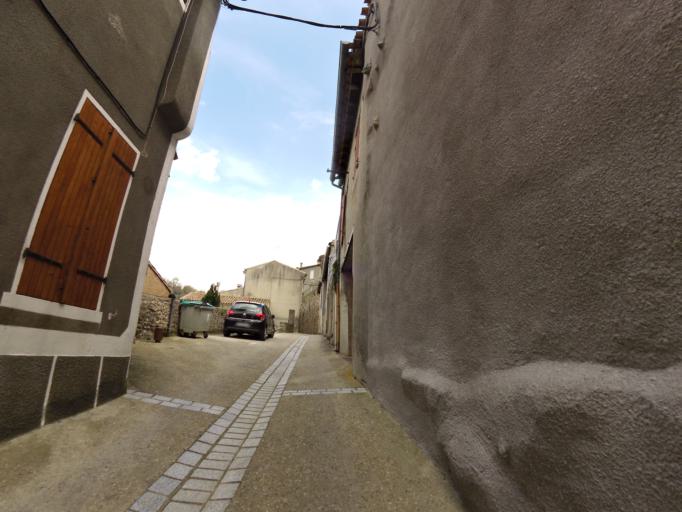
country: FR
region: Languedoc-Roussillon
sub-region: Departement de l'Aude
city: Alzonne
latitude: 43.3589
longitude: 2.1683
